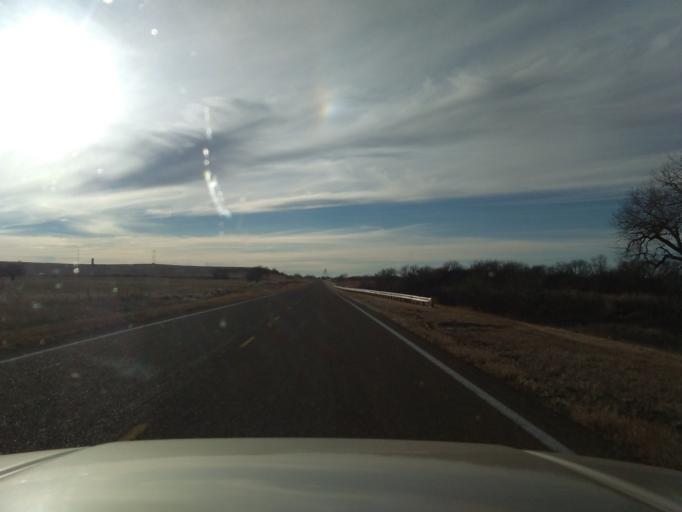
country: US
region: Kansas
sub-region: Norton County
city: Norton
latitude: 39.7452
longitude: -100.1587
